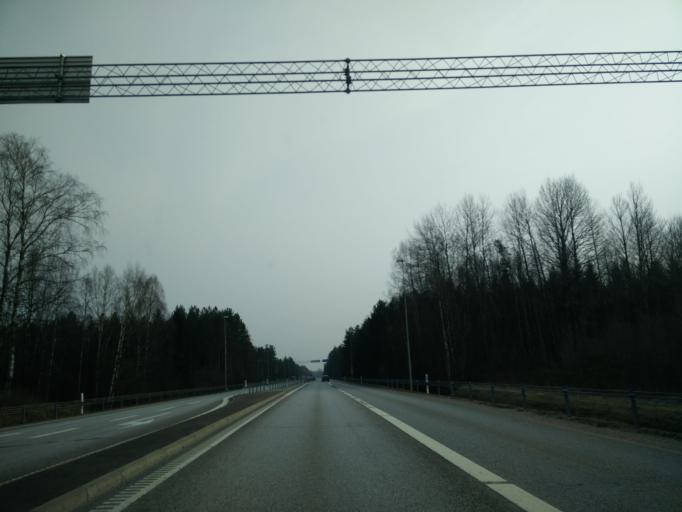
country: SE
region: Vaermland
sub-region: Forshaga Kommun
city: Forshaga
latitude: 59.4576
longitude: 13.4166
